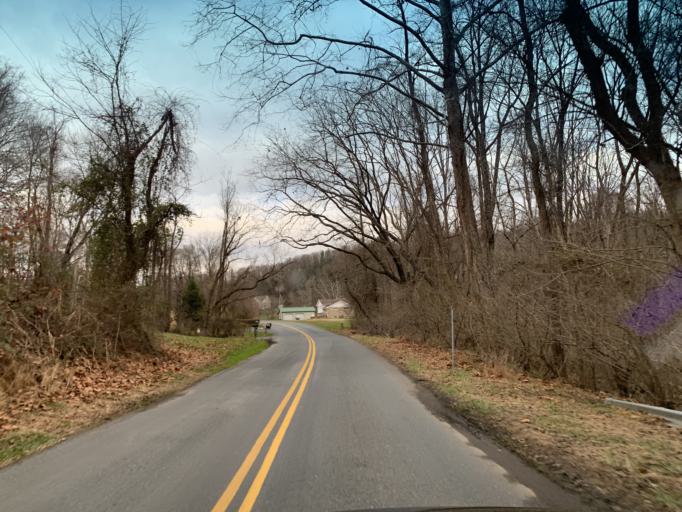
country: US
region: Maryland
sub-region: Harford County
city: Jarrettsville
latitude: 39.6433
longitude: -76.4266
